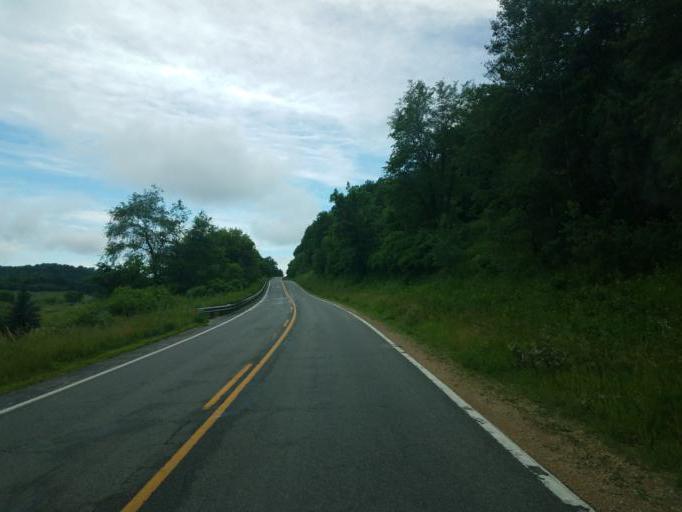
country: US
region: Wisconsin
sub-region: Vernon County
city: Hillsboro
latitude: 43.6606
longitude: -90.4070
